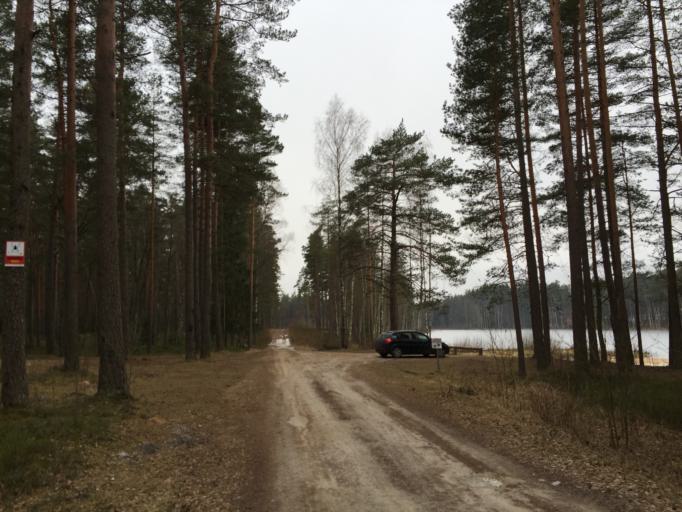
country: LV
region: Garkalne
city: Garkalne
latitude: 56.9608
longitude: 24.4346
